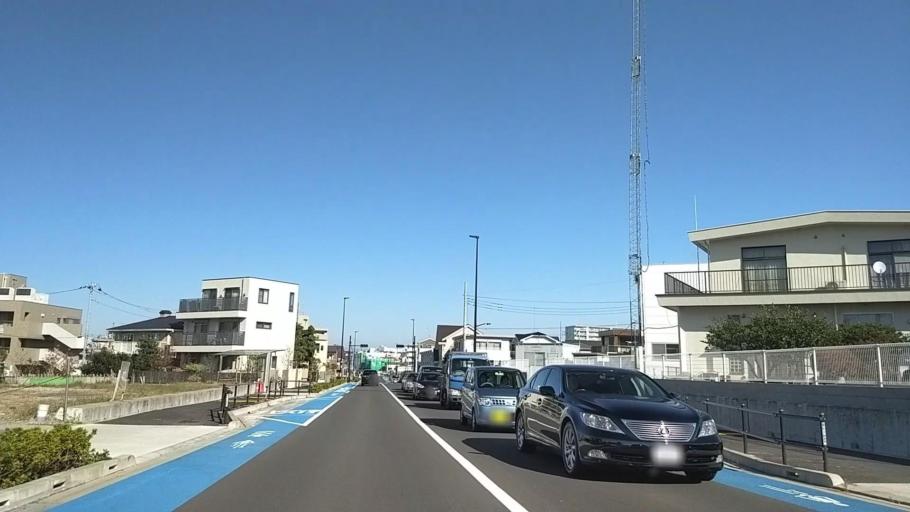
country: JP
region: Tokyo
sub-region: Machida-shi
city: Machida
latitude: 35.5149
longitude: 139.4652
